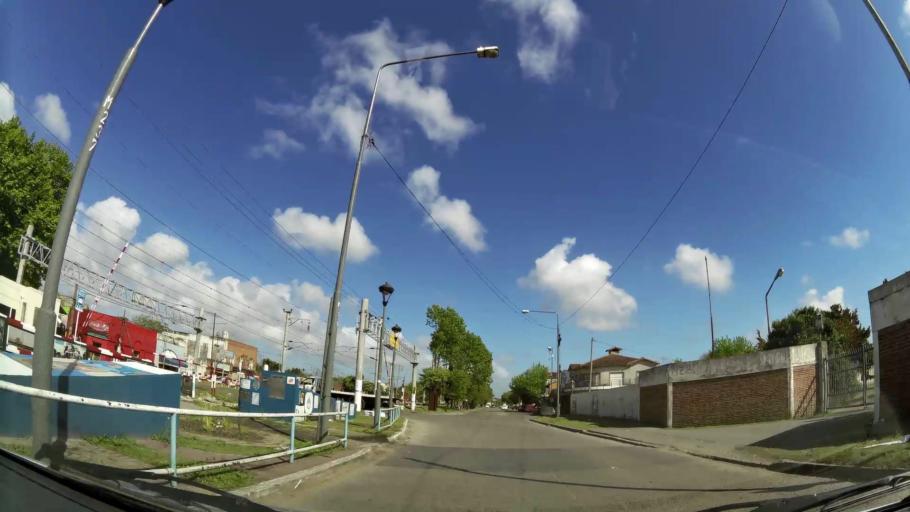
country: AR
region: Buenos Aires
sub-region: Partido de Quilmes
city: Quilmes
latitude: -34.7884
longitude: -58.1600
